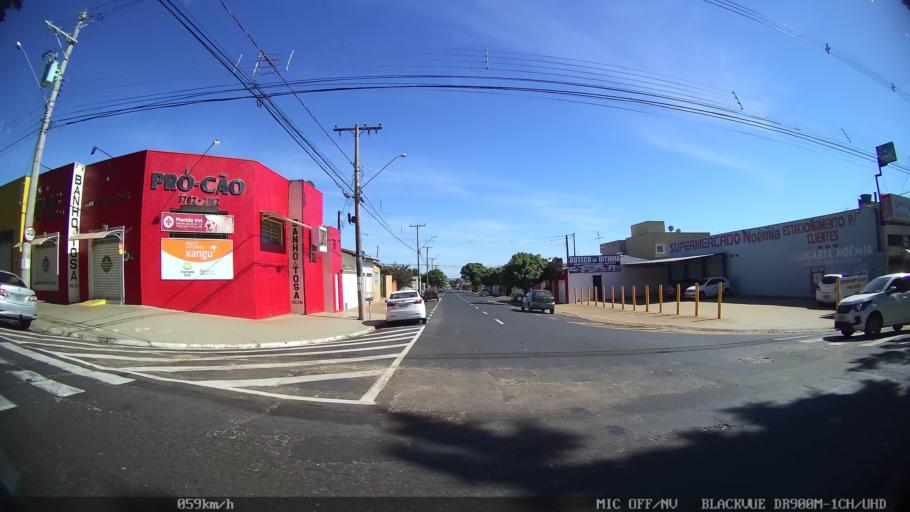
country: BR
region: Sao Paulo
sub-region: Franca
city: Franca
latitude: -20.5571
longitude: -47.3725
